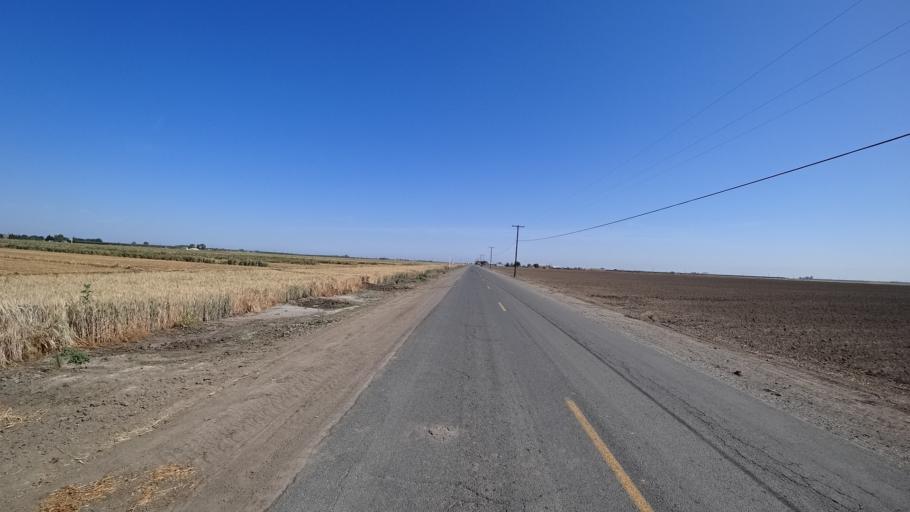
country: US
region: California
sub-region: Kings County
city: Home Garden
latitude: 36.2482
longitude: -119.5474
